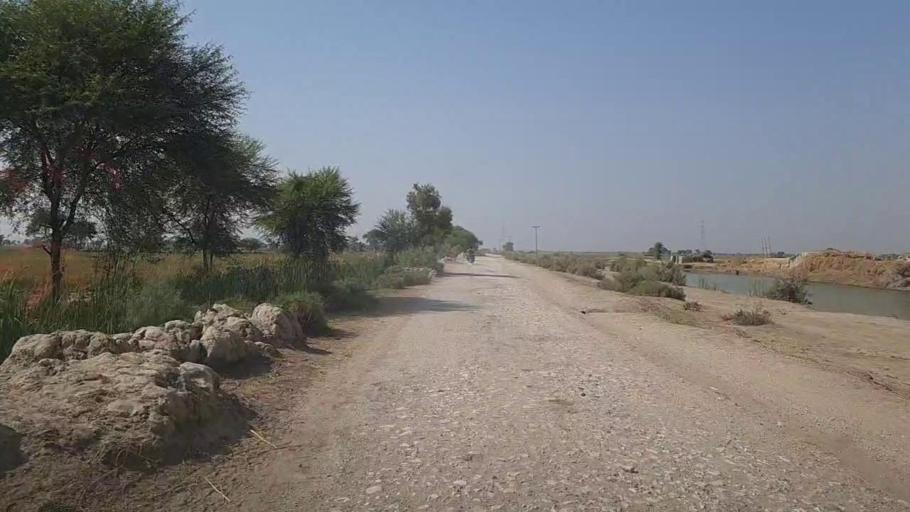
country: PK
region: Sindh
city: Kandhkot
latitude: 28.4059
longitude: 69.2538
